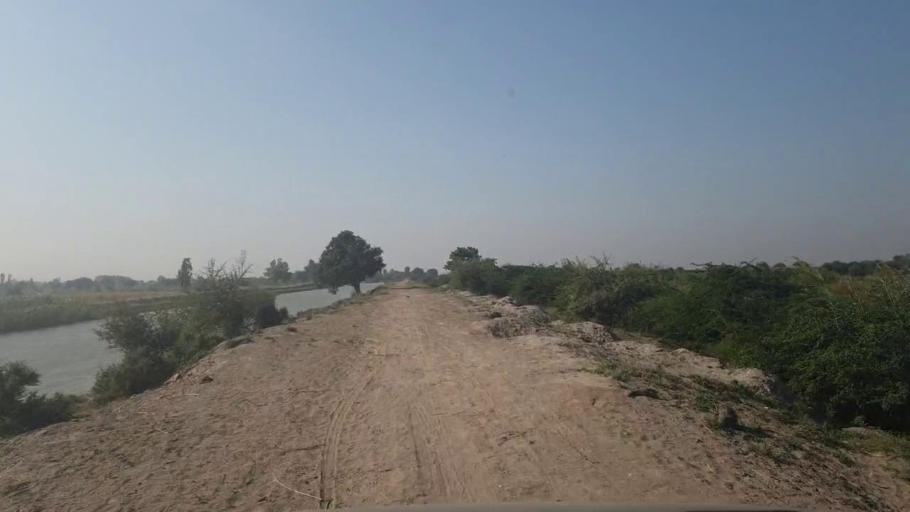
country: PK
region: Sindh
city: Badin
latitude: 24.6911
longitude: 68.8690
